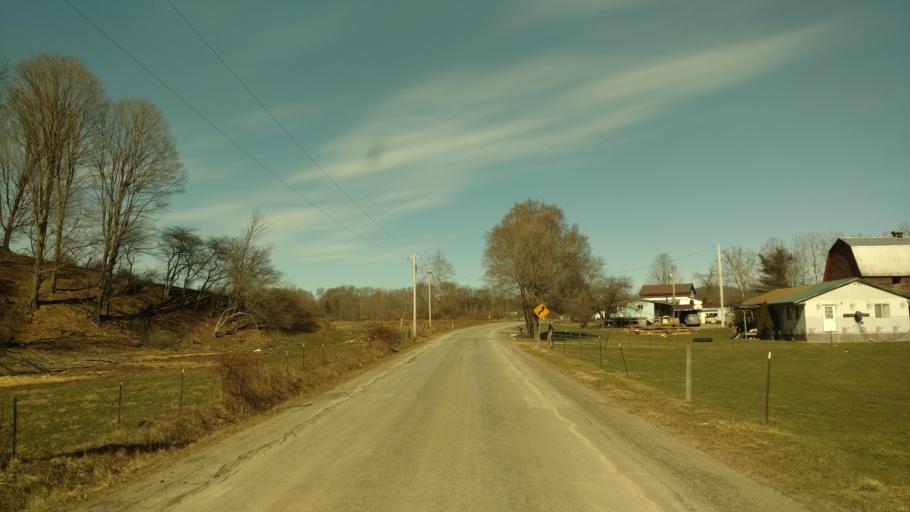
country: US
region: New York
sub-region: Allegany County
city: Wellsville
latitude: 42.0657
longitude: -77.9291
